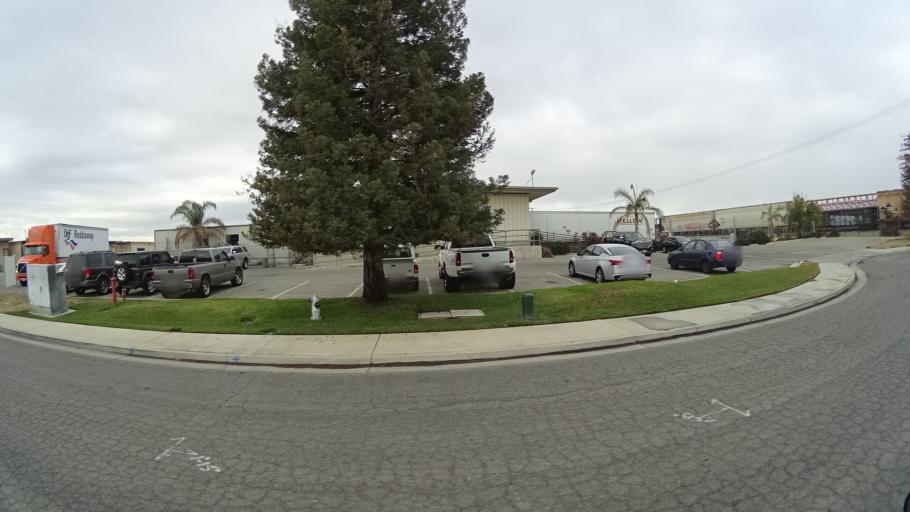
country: US
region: California
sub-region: Kern County
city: Greenfield
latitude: 35.3100
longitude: -119.0621
